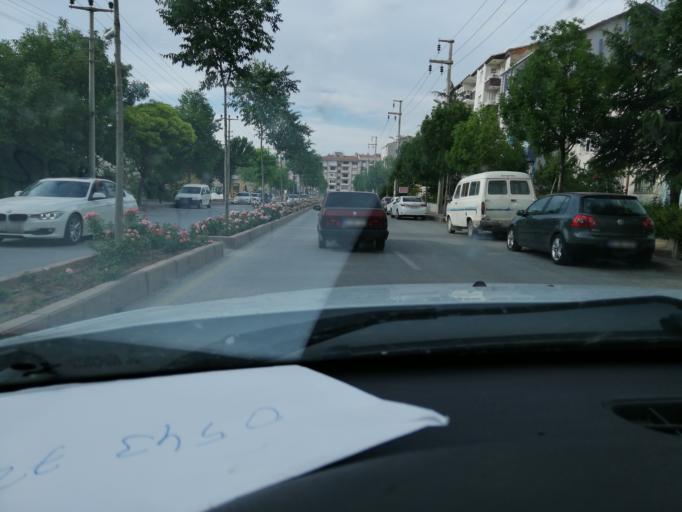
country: TR
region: Kirsehir
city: Kirsehir
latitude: 39.1381
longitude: 34.1600
